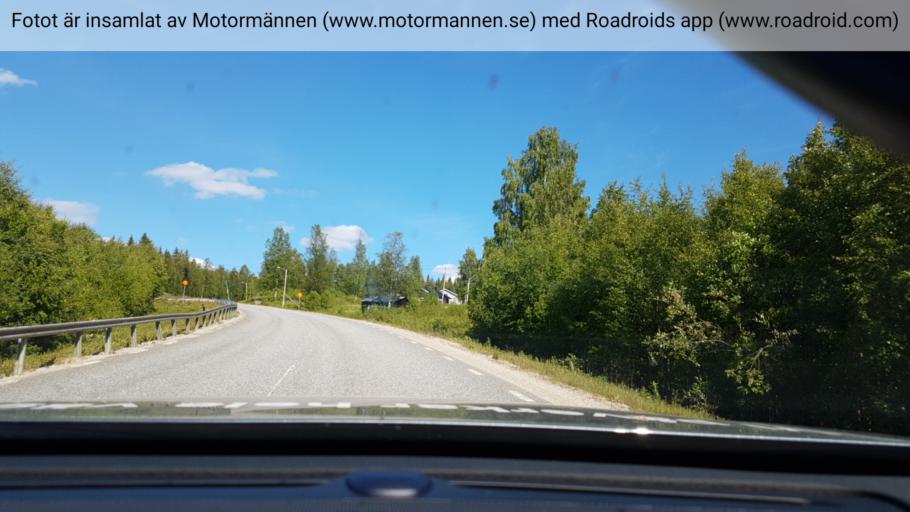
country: SE
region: Vaesterbotten
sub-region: Lycksele Kommun
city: Soderfors
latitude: 64.6173
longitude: 18.3248
